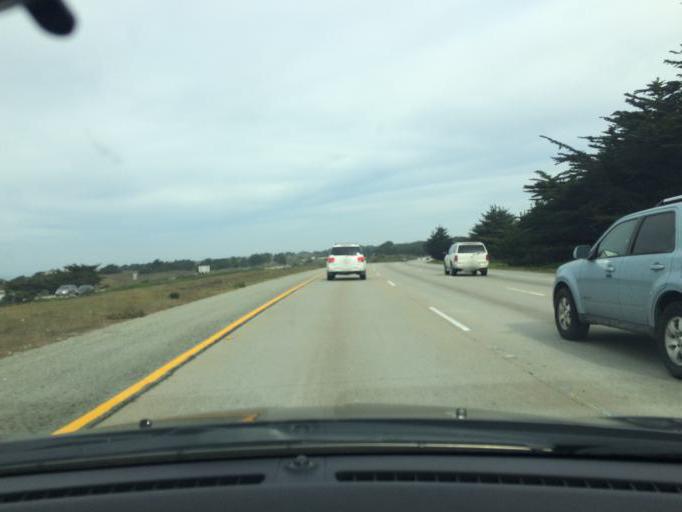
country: US
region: California
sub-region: Monterey County
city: Seaside
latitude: 36.6361
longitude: -121.8306
